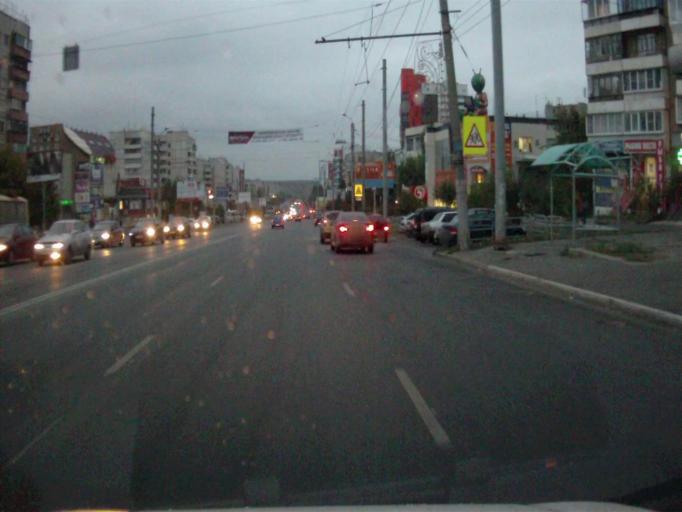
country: RU
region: Chelyabinsk
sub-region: Gorod Chelyabinsk
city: Chelyabinsk
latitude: 55.1881
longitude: 61.3326
